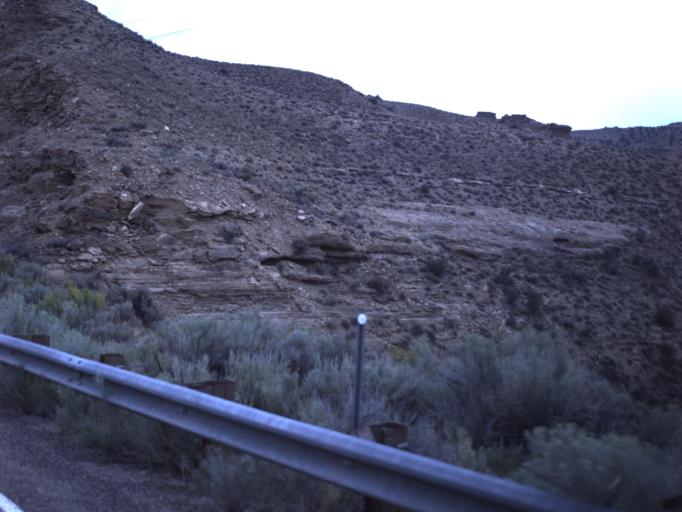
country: US
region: Colorado
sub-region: Rio Blanco County
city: Rangely
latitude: 39.9875
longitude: -109.1776
